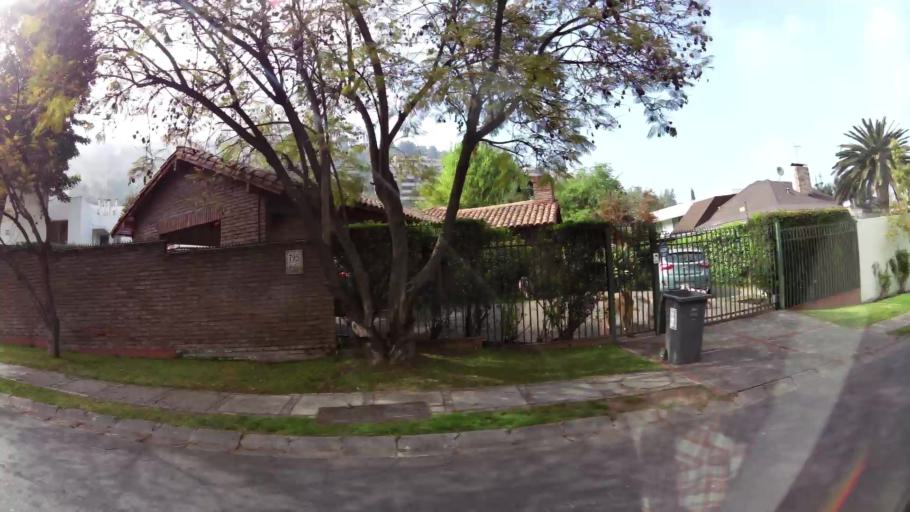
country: CL
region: Santiago Metropolitan
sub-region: Provincia de Santiago
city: Villa Presidente Frei, Nunoa, Santiago, Chile
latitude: -33.3696
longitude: -70.5721
